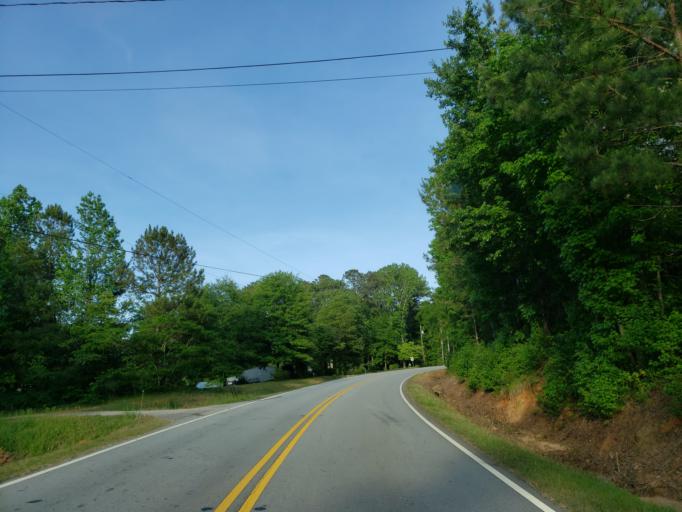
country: US
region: Georgia
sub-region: Carroll County
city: Mount Zion
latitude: 33.6374
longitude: -85.1947
